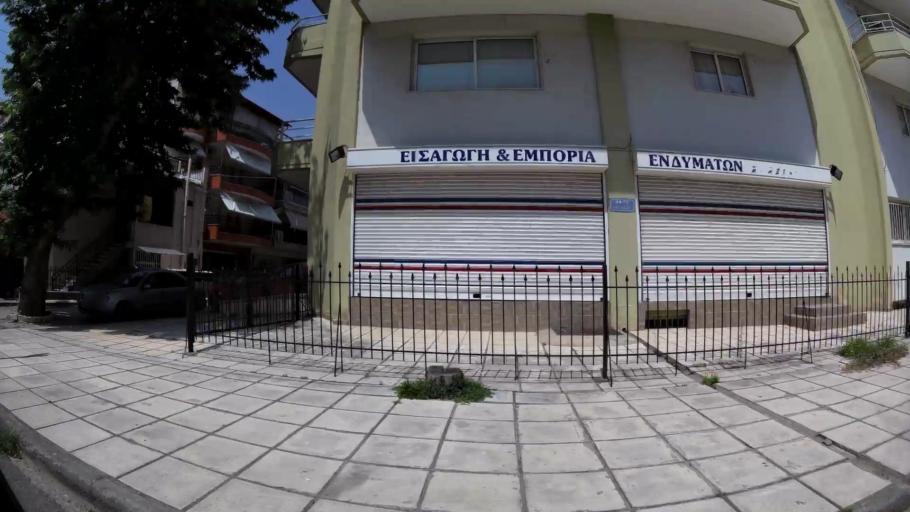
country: GR
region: Central Macedonia
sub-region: Nomos Thessalonikis
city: Menemeni
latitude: 40.6594
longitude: 22.9037
